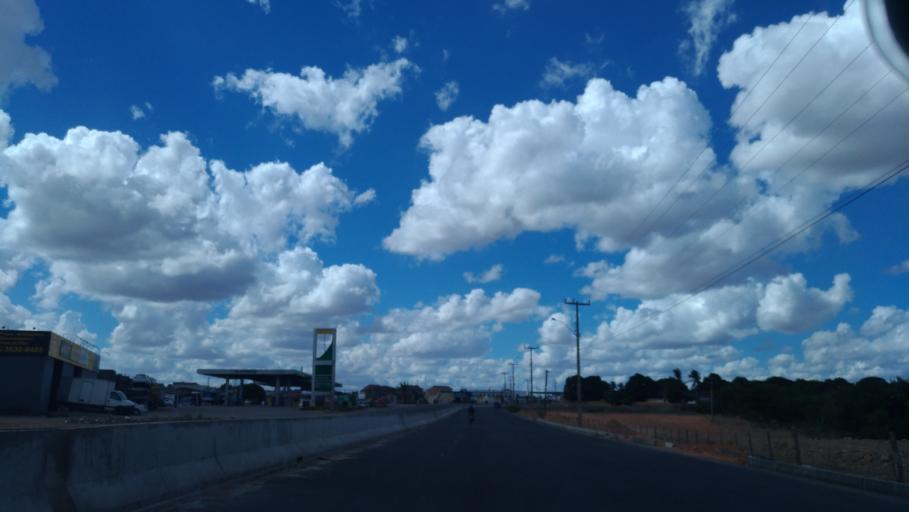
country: BR
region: Alagoas
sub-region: Arapiraca
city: Arapiraca
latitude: -9.7555
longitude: -36.6390
